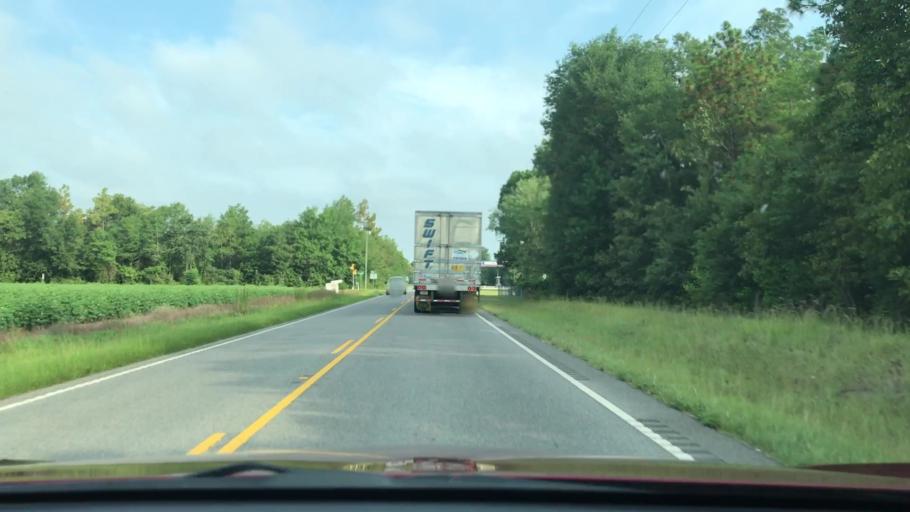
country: US
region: South Carolina
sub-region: Barnwell County
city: Williston
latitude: 33.6271
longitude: -81.3000
